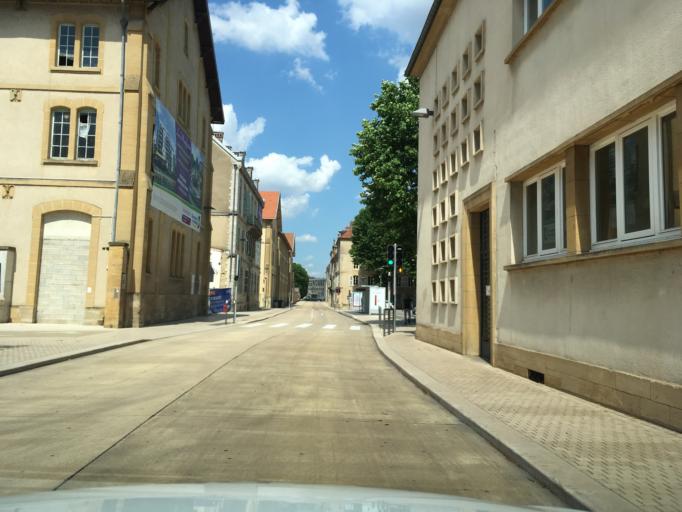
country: FR
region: Lorraine
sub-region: Departement de la Moselle
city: Metz
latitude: 49.1235
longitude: 6.1716
